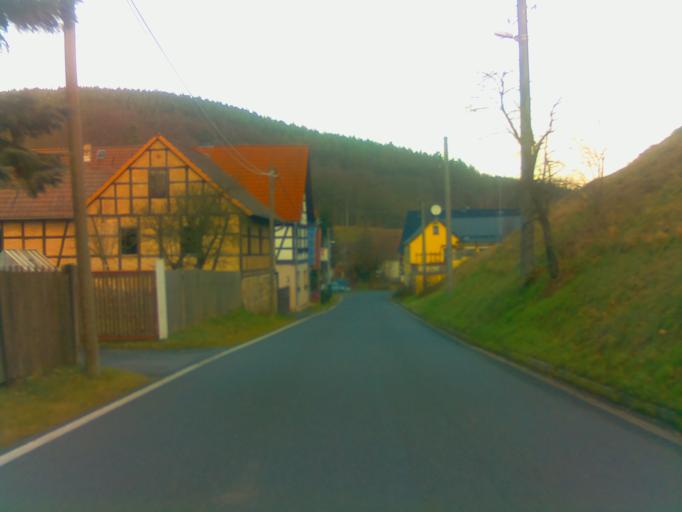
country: DE
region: Thuringia
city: Saalfeld
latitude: 50.6960
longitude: 11.3977
